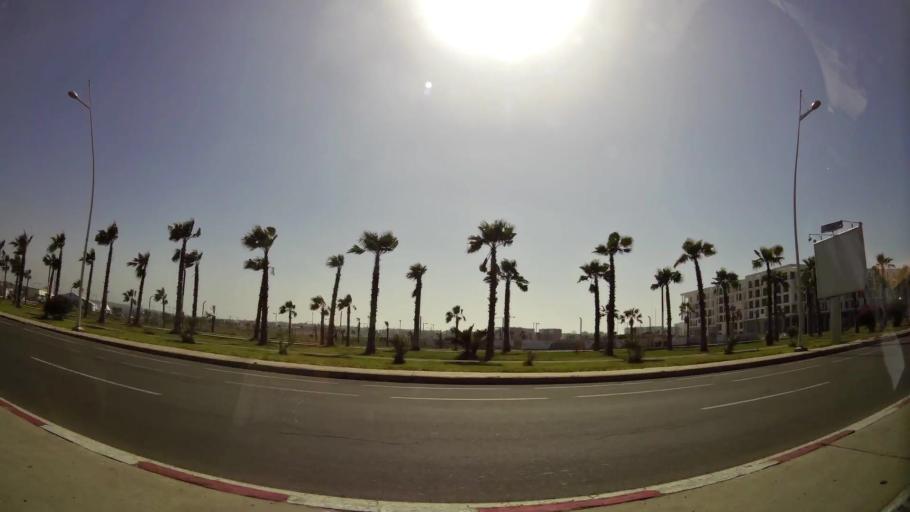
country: MA
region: Souss-Massa-Draa
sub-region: Agadir-Ida-ou-Tnan
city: Agadir
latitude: 30.3986
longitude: -9.5821
